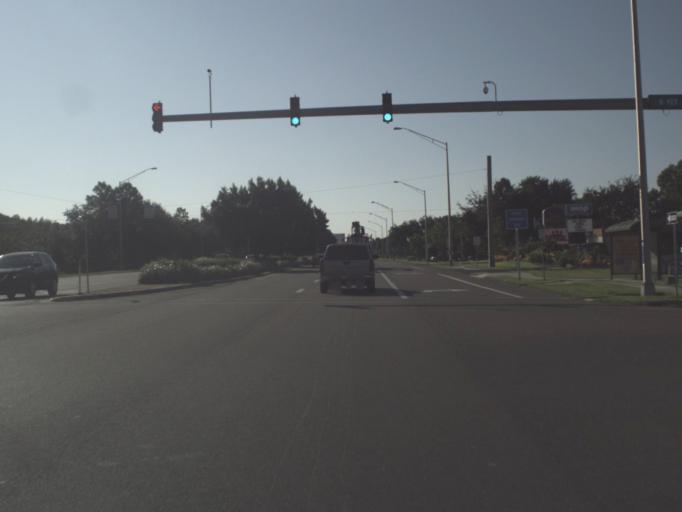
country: US
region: Florida
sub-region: Lee County
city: North Fort Myers
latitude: 26.6597
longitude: -81.8838
